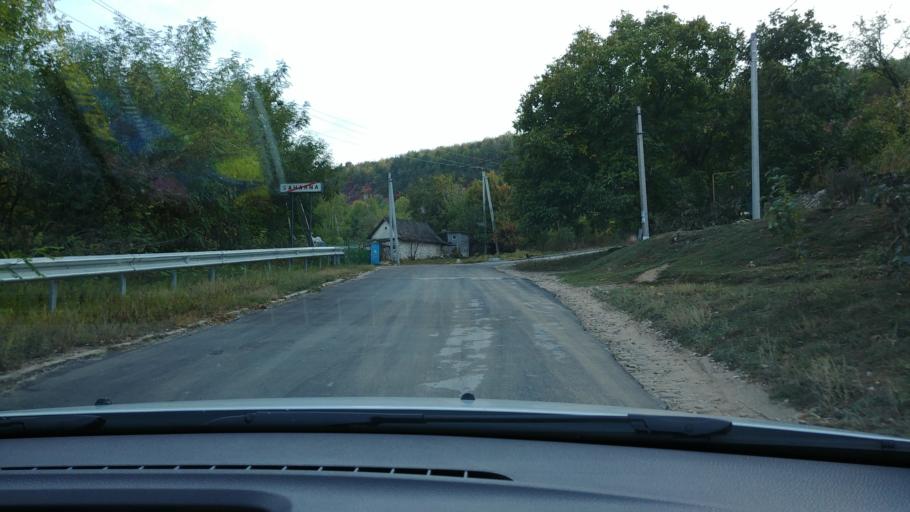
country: MD
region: Rezina
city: Saharna
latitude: 47.6885
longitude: 28.9745
